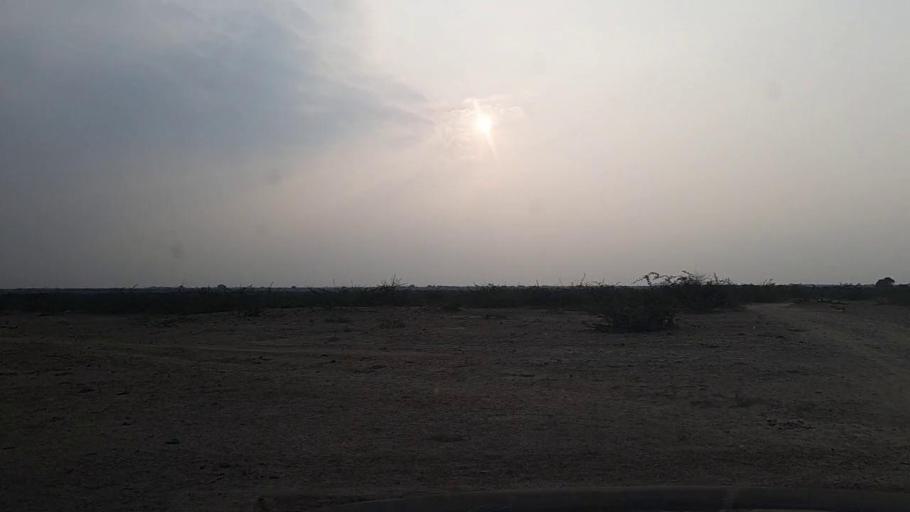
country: PK
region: Sindh
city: Gharo
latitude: 24.7715
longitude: 67.6924
